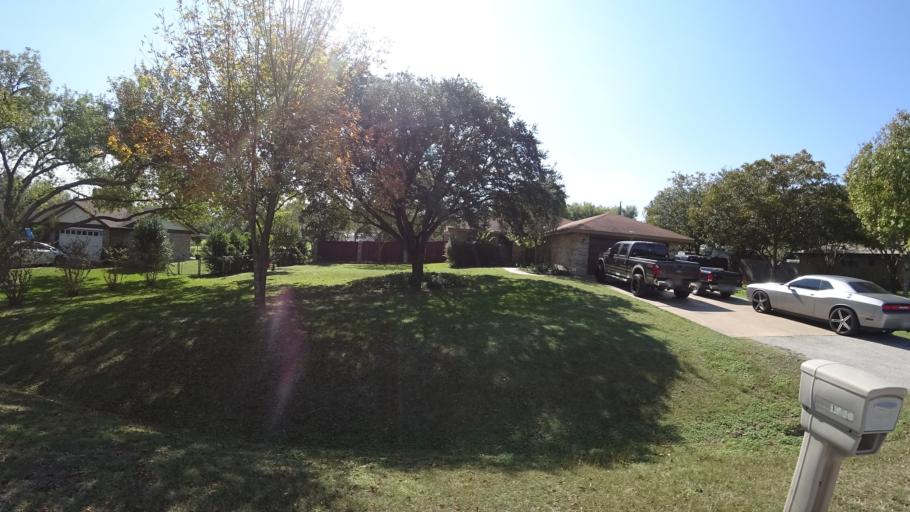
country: US
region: Texas
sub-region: Travis County
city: Pflugerville
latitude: 30.4188
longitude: -97.6262
